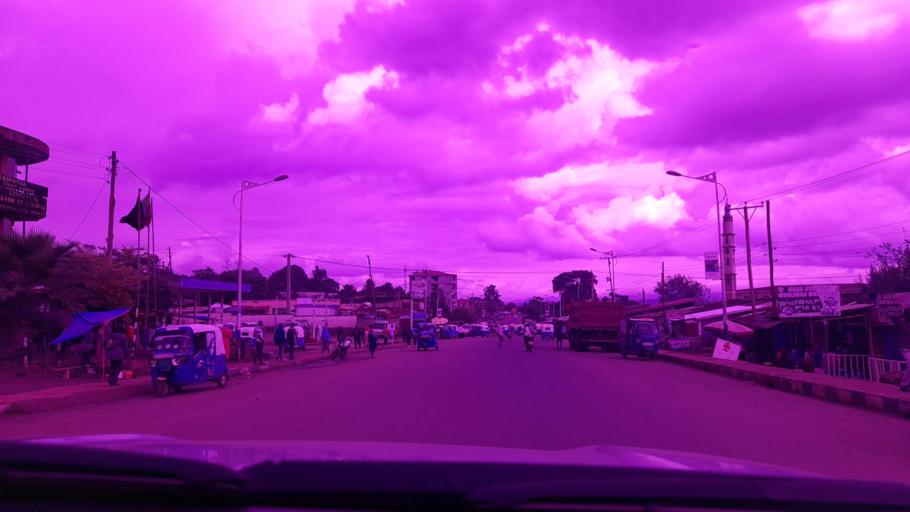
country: ET
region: Oromiya
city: Jima
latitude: 7.6735
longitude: 36.8540
